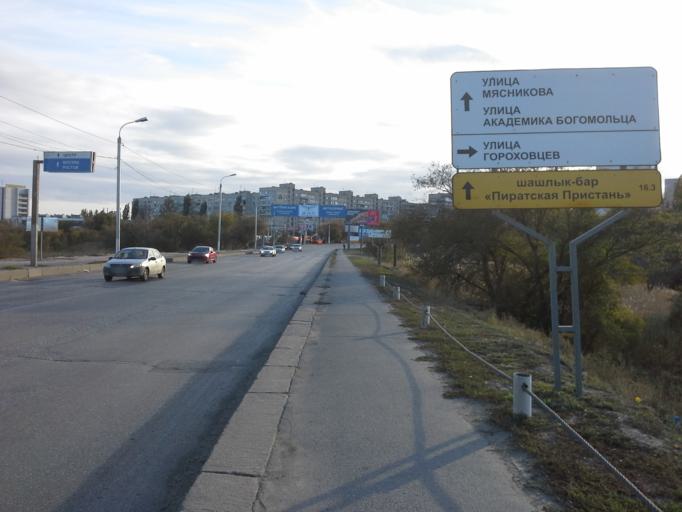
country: RU
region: Volgograd
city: Vodstroy
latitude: 48.8260
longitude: 44.6422
